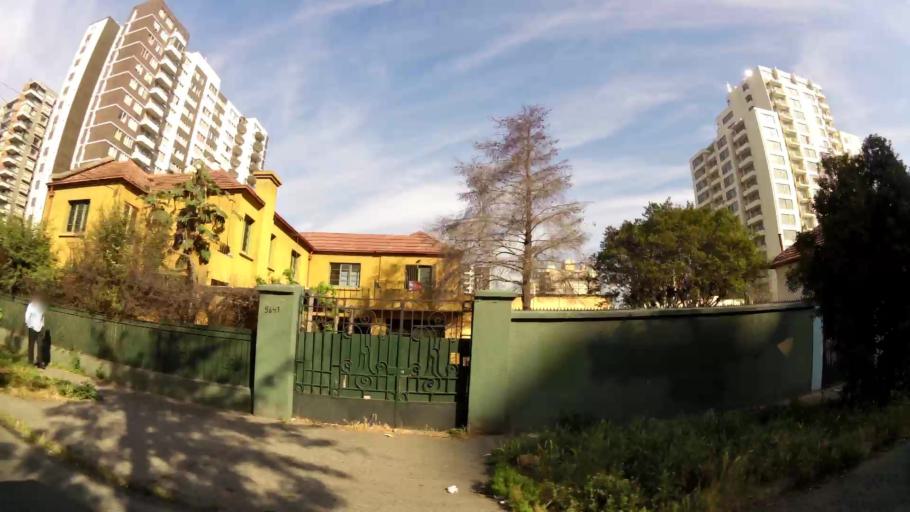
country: CL
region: Santiago Metropolitan
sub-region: Provincia de Santiago
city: Santiago
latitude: -33.5052
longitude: -70.6578
